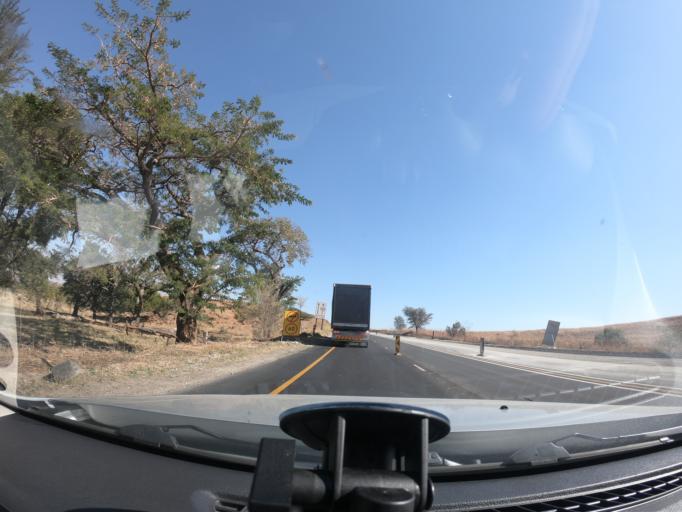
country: ZA
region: KwaZulu-Natal
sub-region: uThukela District Municipality
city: Bergville
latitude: -28.4345
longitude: 29.4728
